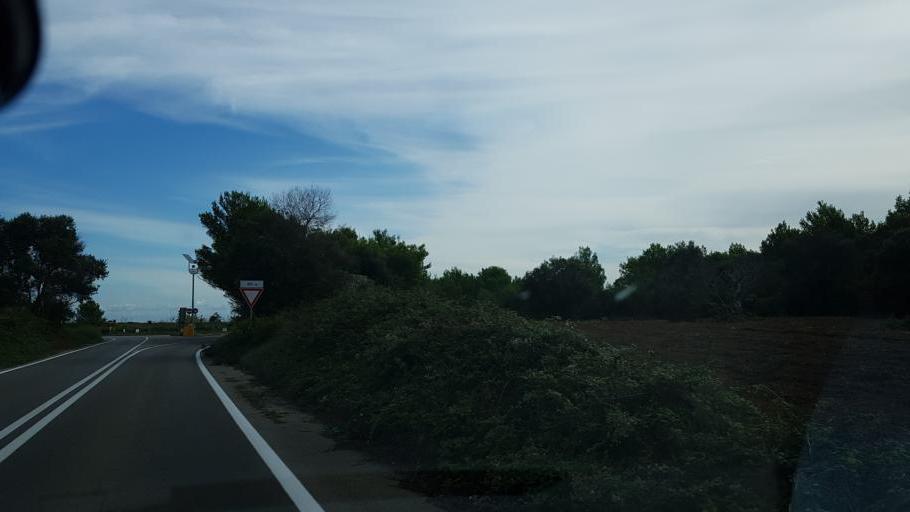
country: IT
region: Apulia
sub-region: Provincia di Lecce
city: Melendugno
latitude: 40.3385
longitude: 18.3541
